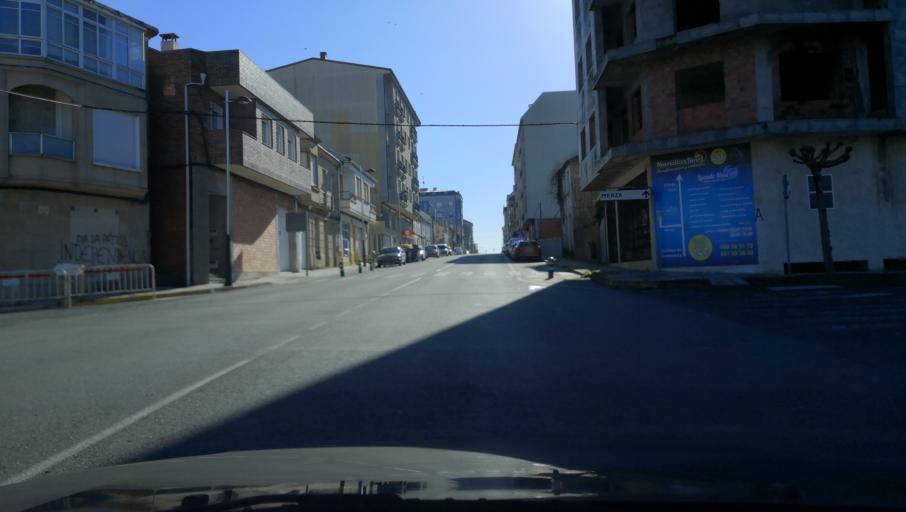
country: ES
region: Galicia
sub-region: Provincia de Pontevedra
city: Silleda
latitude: 42.7312
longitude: -8.3060
